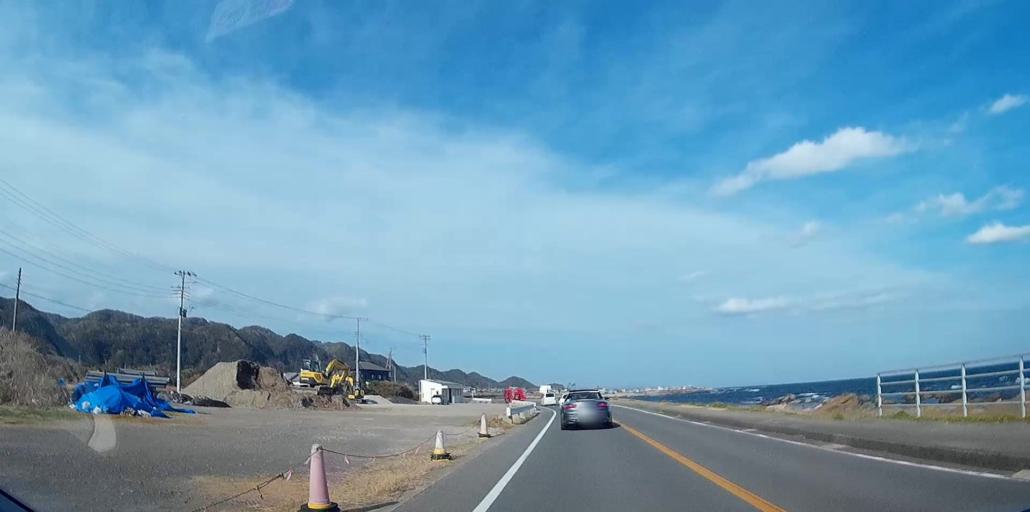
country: JP
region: Chiba
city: Tateyama
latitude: 34.9190
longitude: 139.9414
